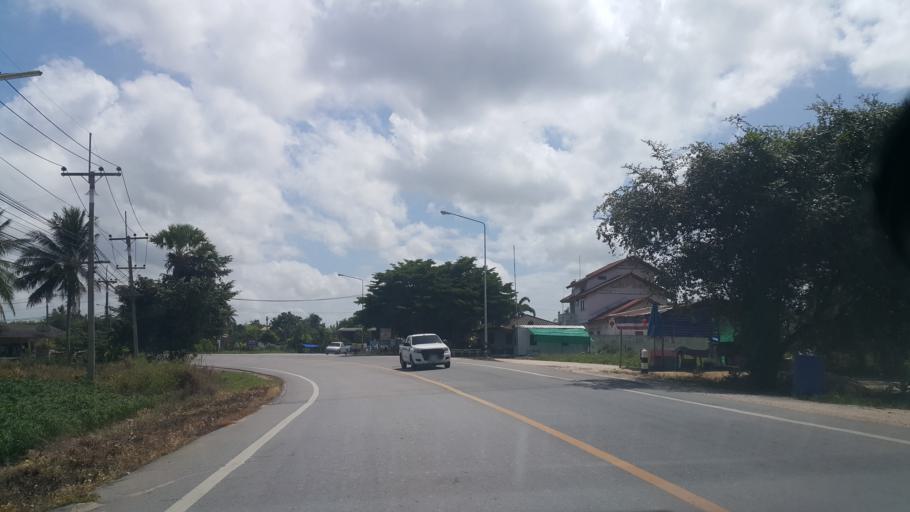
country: TH
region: Rayong
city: Ban Chang
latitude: 12.7917
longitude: 101.0319
